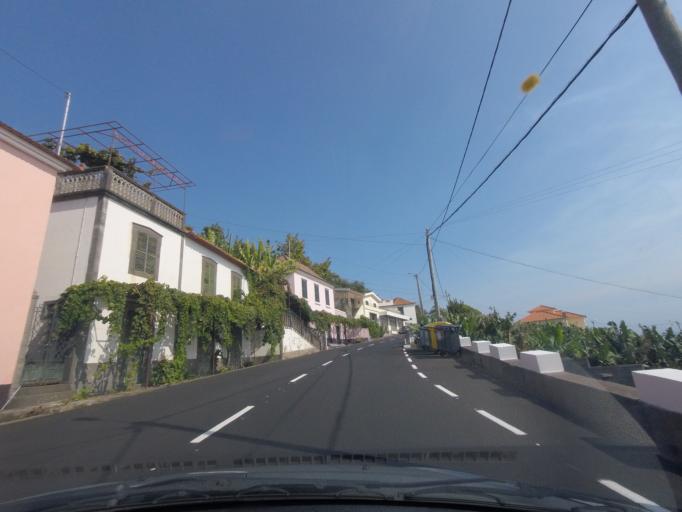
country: PT
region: Madeira
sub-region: Ribeira Brava
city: Campanario
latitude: 32.6697
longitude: -17.0555
